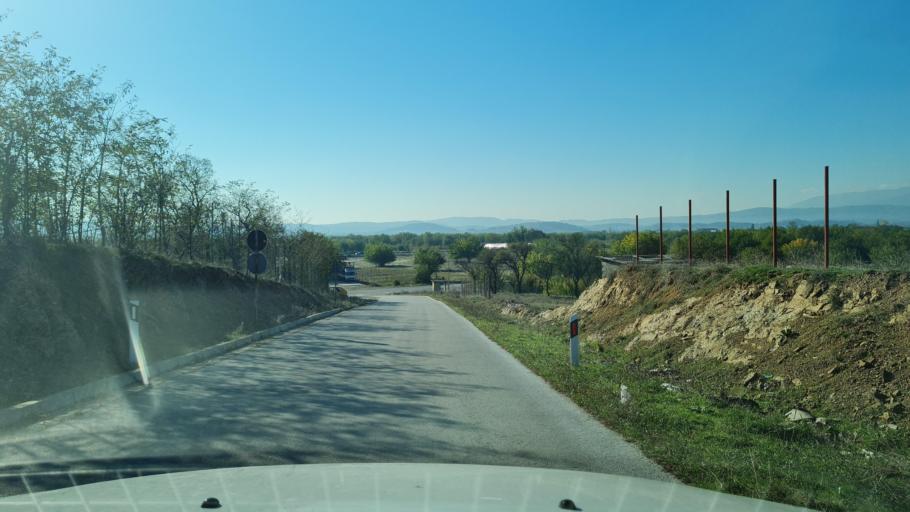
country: MK
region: Bogdanci
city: Bogdanci
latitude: 41.1936
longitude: 22.5632
